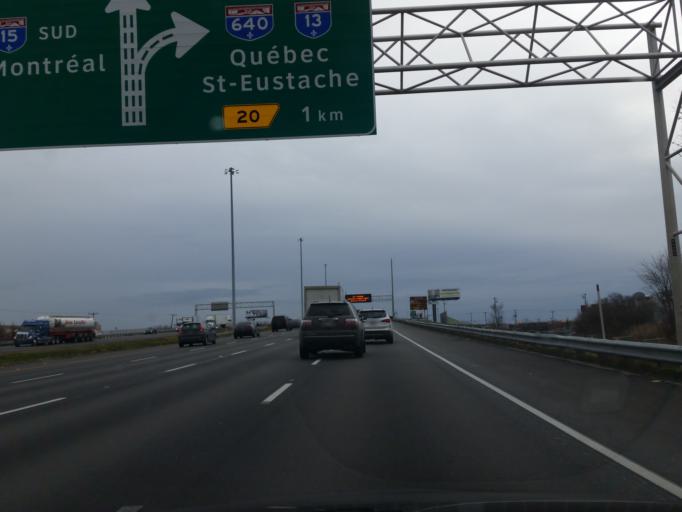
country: CA
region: Quebec
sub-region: Laurentides
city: Sainte-Therese
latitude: 45.6381
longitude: -73.8565
